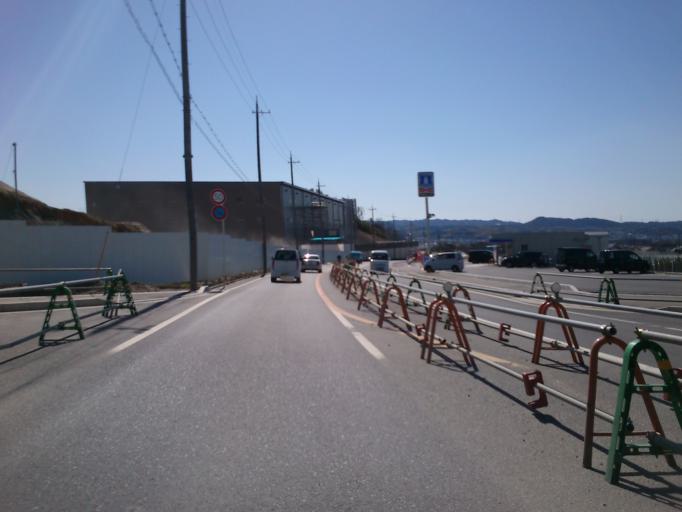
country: JP
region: Kyoto
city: Tanabe
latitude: 34.8247
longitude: 135.8126
